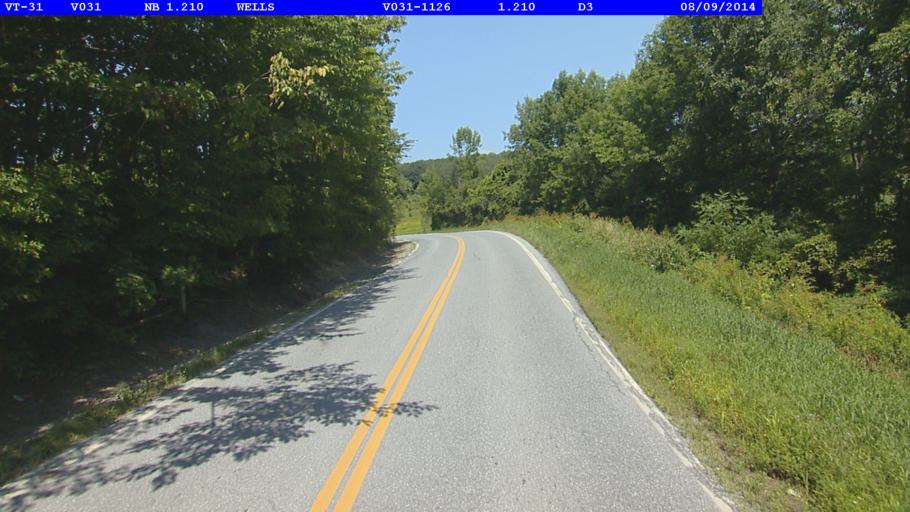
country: US
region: New York
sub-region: Washington County
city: Granville
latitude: 43.4546
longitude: -73.2421
